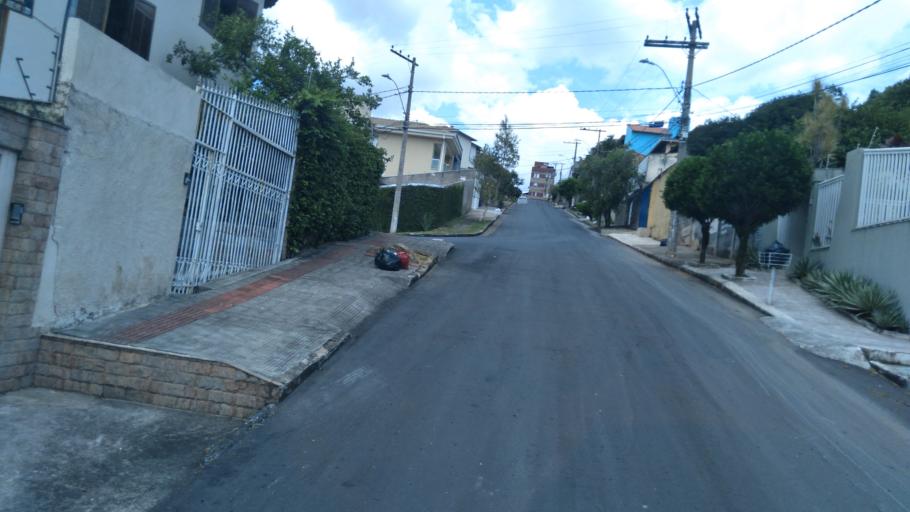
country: BR
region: Minas Gerais
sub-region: Contagem
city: Contagem
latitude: -19.9145
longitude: -44.0079
